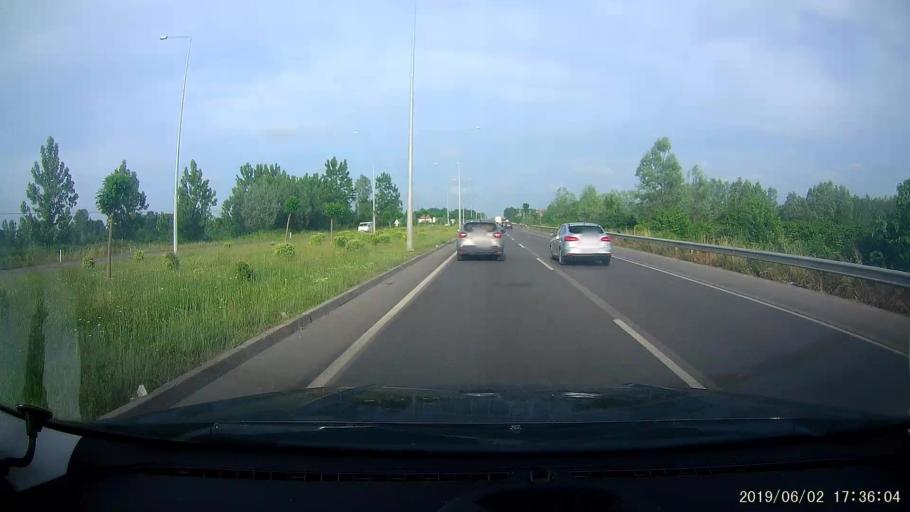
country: TR
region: Samsun
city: Terme
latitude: 41.2191
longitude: 36.8925
